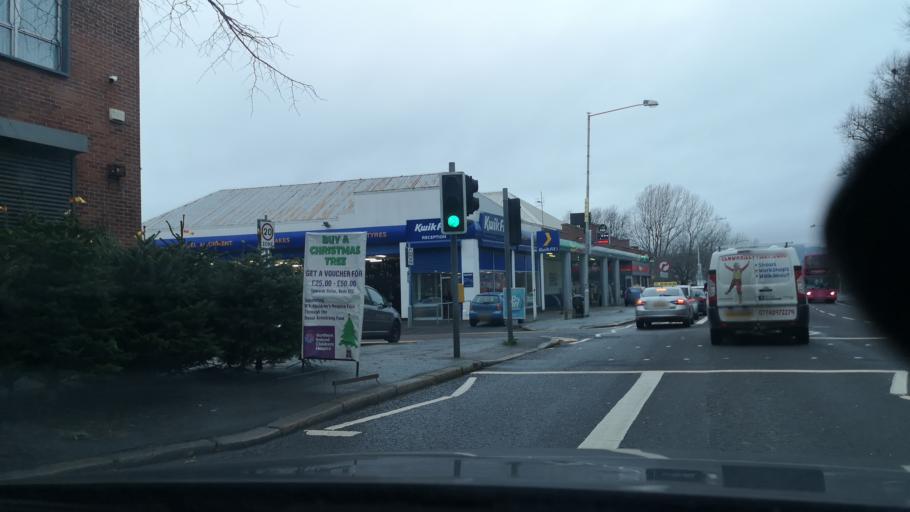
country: GB
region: Northern Ireland
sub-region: City of Belfast
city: Belfast
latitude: 54.5812
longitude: -5.9212
